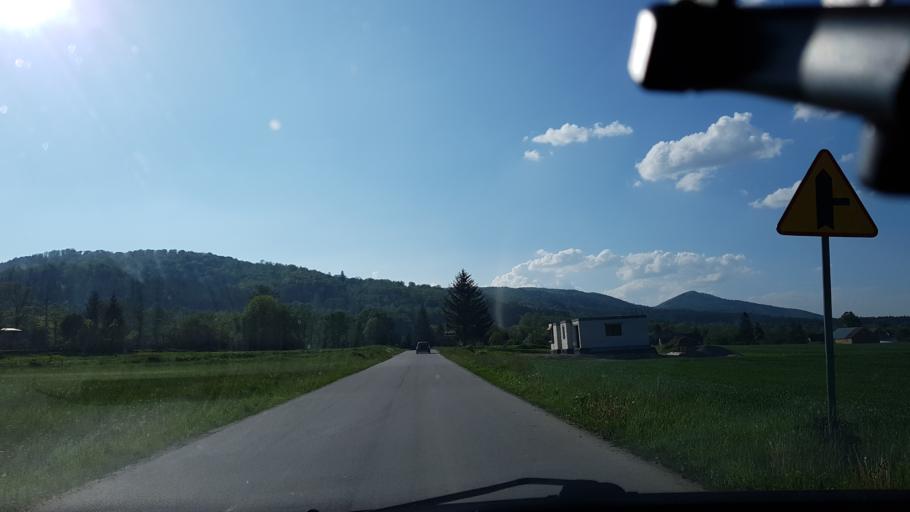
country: PL
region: Lower Silesian Voivodeship
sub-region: Powiat zabkowicki
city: Budzow
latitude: 50.5920
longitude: 16.6566
